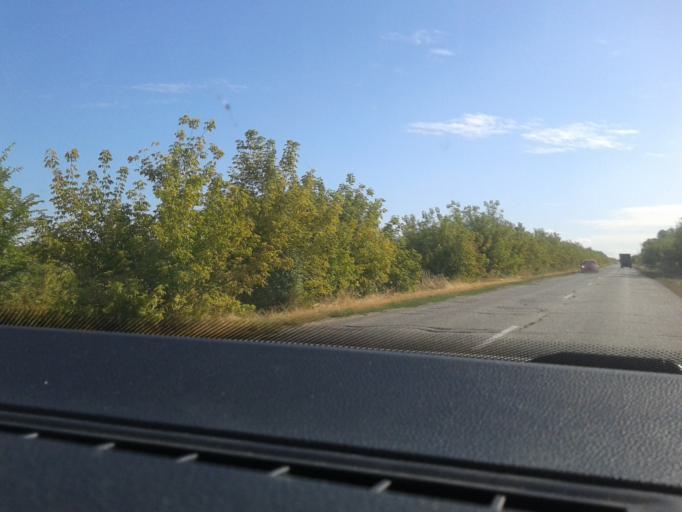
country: RU
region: Volgograd
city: Frolovo
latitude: 49.7687
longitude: 43.5695
